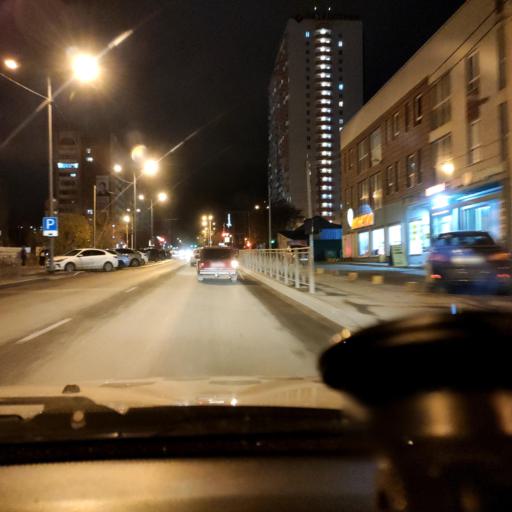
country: RU
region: Perm
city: Perm
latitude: 57.9783
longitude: 56.2032
